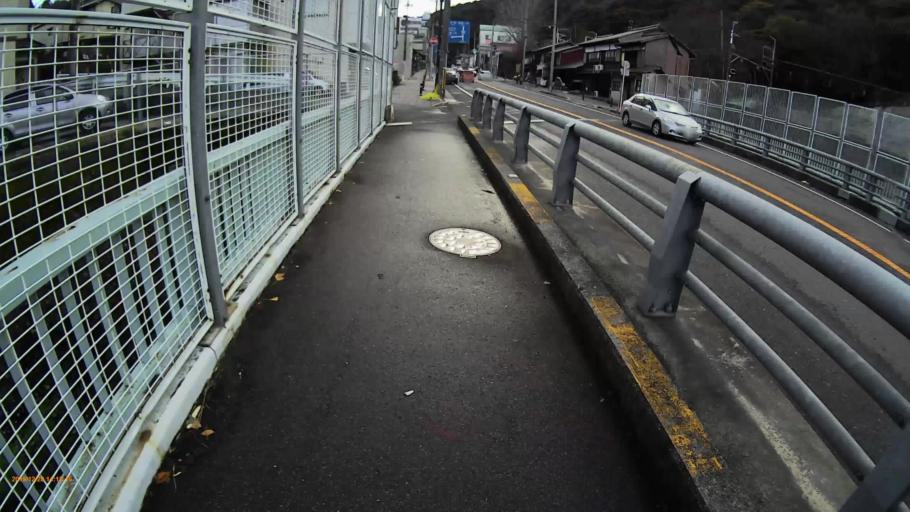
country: JP
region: Shiga Prefecture
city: Otsu-shi
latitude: 35.0032
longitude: 135.8602
